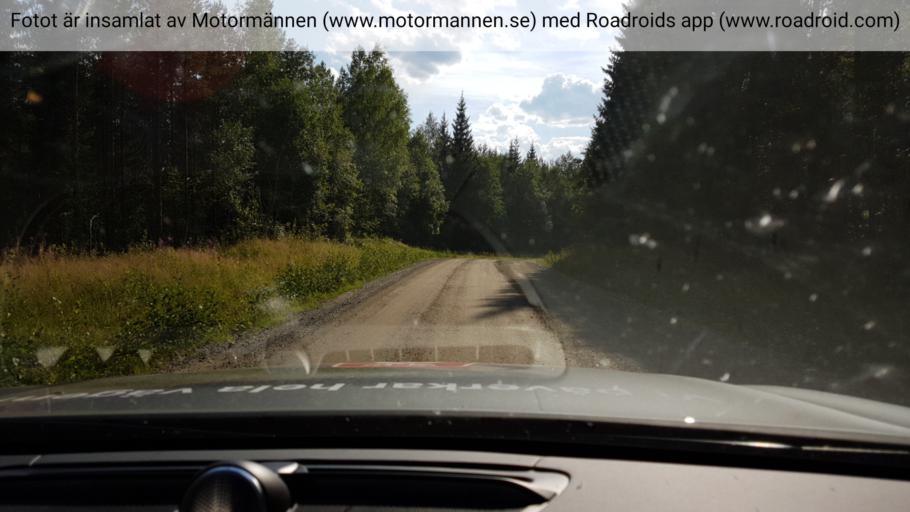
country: SE
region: Vaesternorrland
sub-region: Solleftea Kommun
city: As
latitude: 63.7813
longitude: 16.3607
